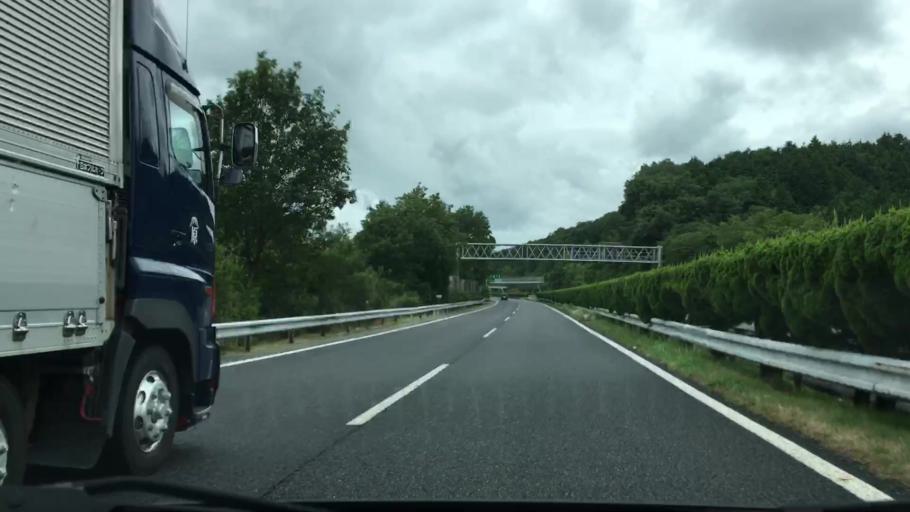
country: JP
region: Okayama
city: Tsuyama
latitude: 35.0384
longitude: 134.1295
